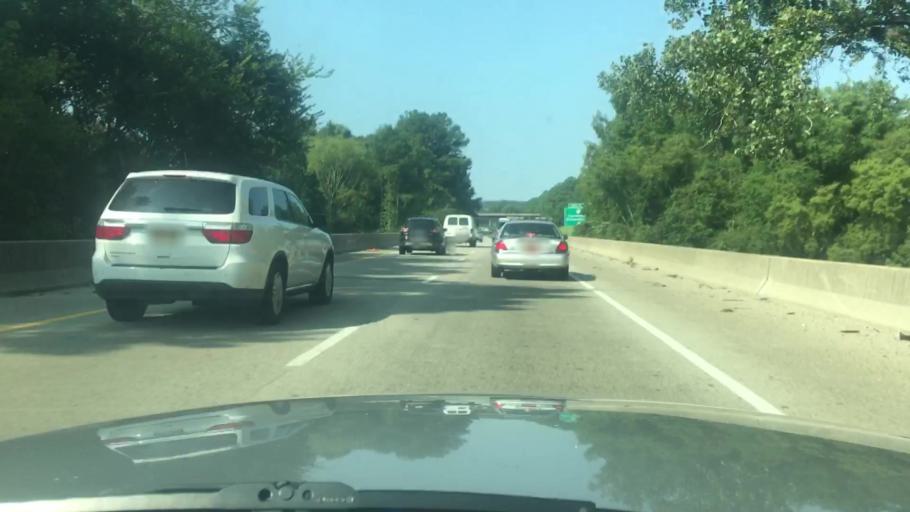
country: US
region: North Carolina
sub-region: Cumberland County
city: Vander
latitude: 34.9827
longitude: -78.8473
